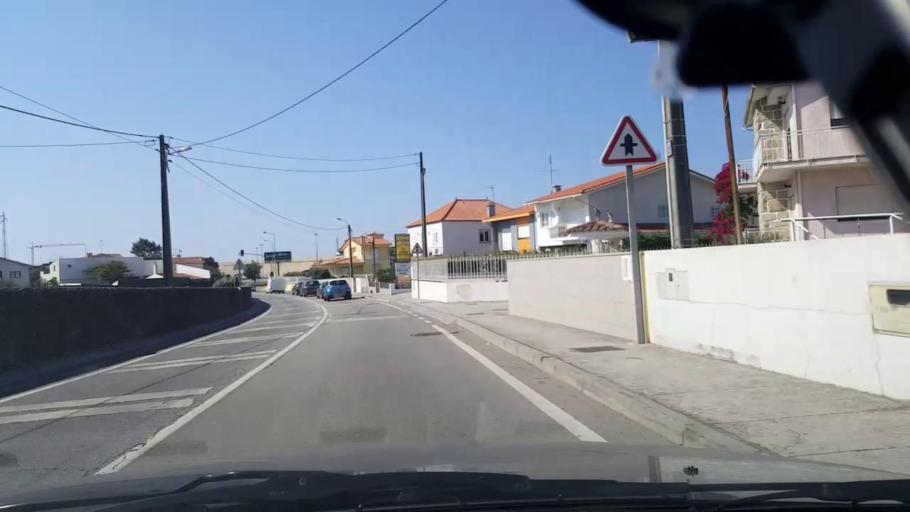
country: PT
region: Porto
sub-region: Vila do Conde
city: Vila do Conde
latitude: 41.3801
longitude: -8.7341
